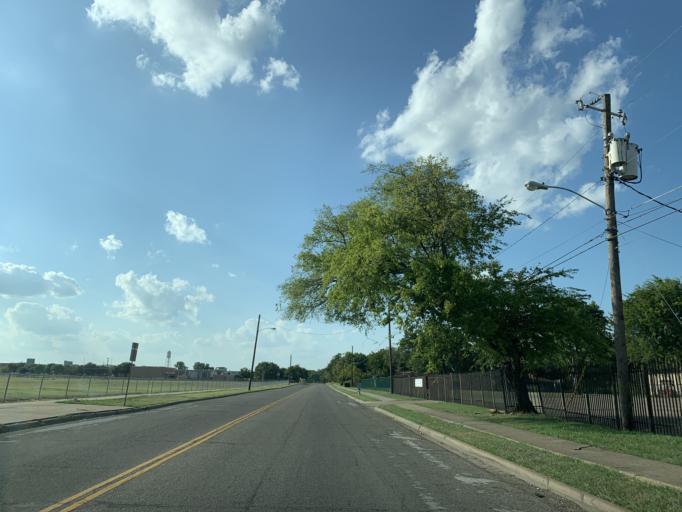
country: US
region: Texas
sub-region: Dallas County
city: Hutchins
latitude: 32.6909
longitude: -96.7805
